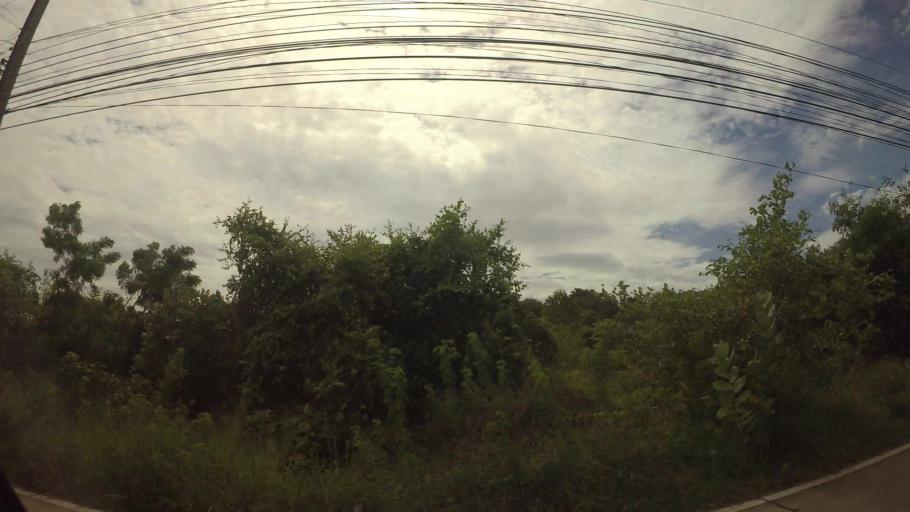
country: TH
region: Rayong
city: Rayong
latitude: 12.6644
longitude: 101.2844
